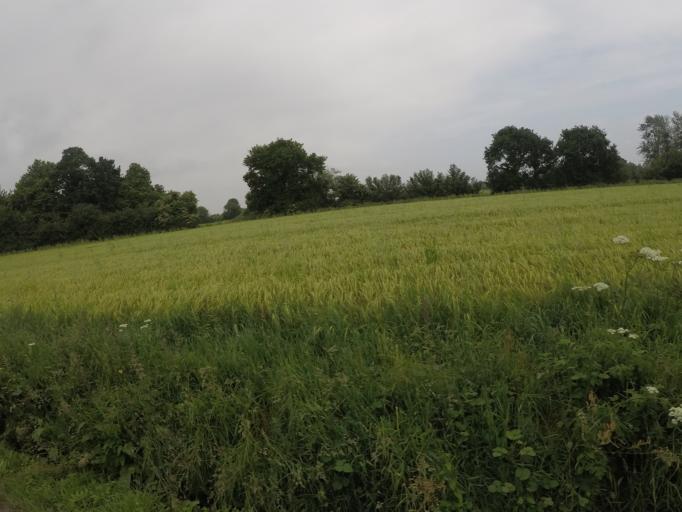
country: FR
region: Brittany
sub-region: Departement des Cotes-d'Armor
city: Pommerit-le-Vicomte
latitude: 48.6382
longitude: -3.0490
